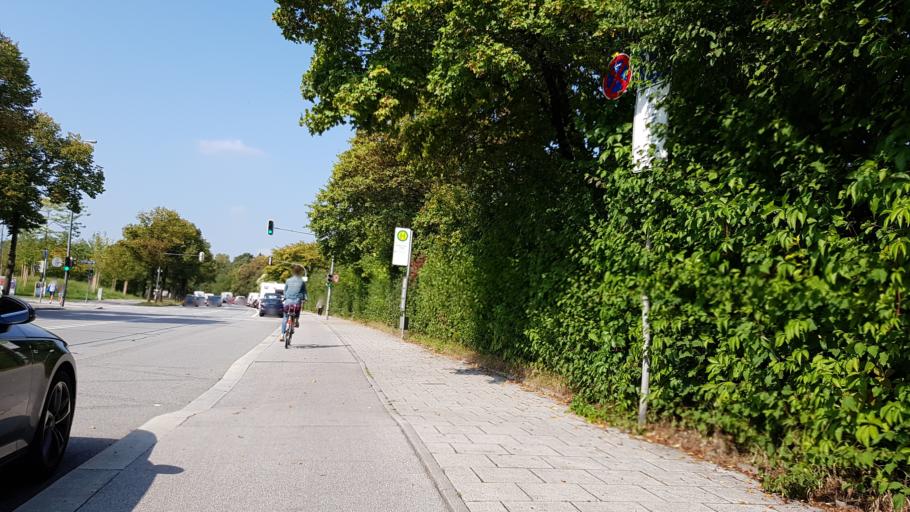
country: DE
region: Bavaria
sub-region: Upper Bavaria
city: Munich
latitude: 48.1687
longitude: 11.5601
